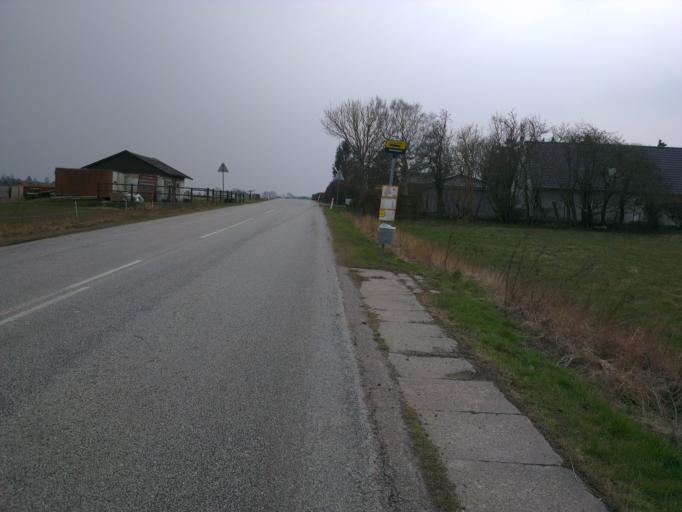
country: DK
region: Capital Region
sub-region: Egedal Kommune
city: Olstykke
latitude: 55.8046
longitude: 12.1099
